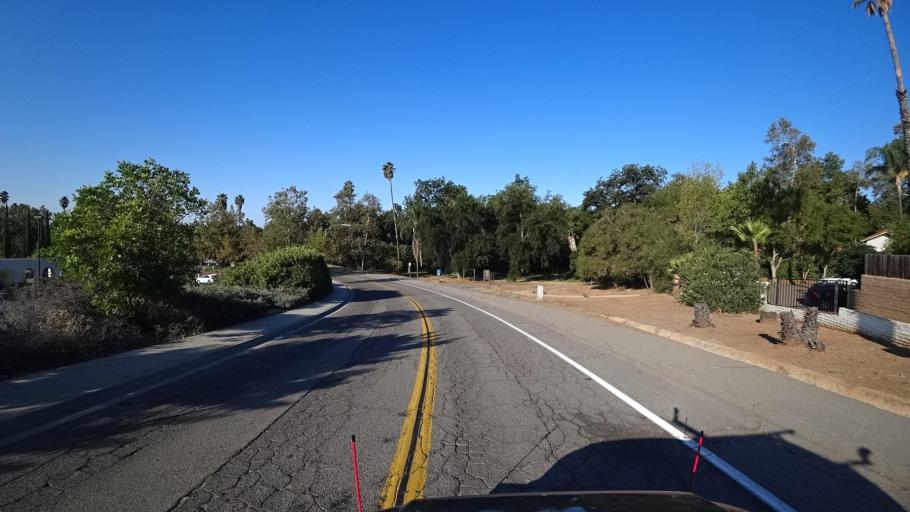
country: US
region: California
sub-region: San Diego County
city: Escondido
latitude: 33.0860
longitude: -117.0607
